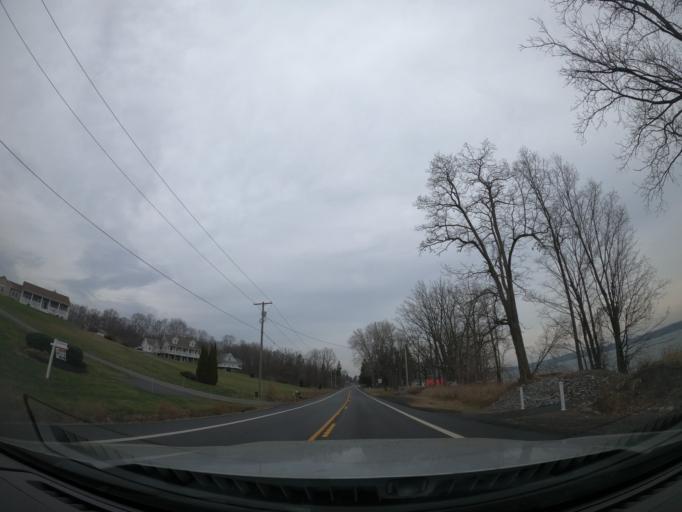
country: US
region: New York
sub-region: Cayuga County
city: Melrose Park
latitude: 42.8434
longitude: -76.5274
